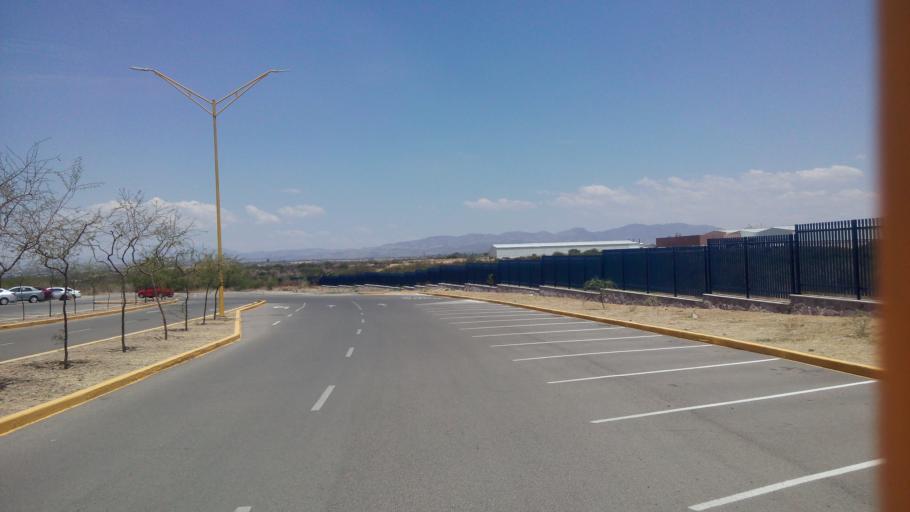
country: MX
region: Aguascalientes
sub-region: Aguascalientes
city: San Sebastian [Fraccionamiento]
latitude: 21.7942
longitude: -102.2918
